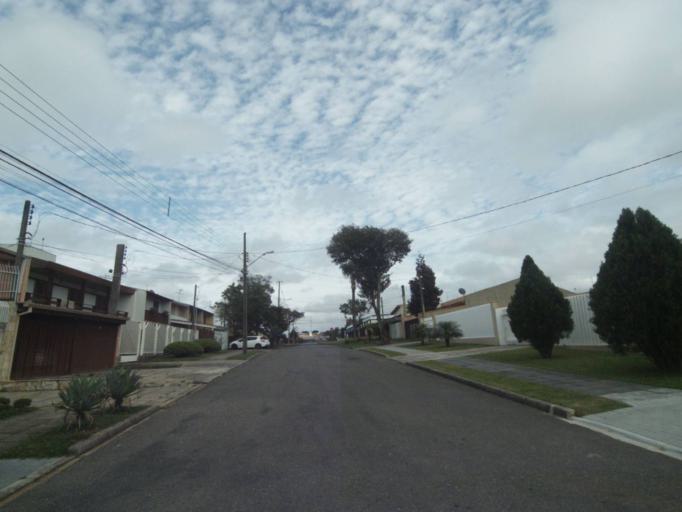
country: BR
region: Parana
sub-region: Pinhais
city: Pinhais
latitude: -25.4338
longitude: -49.2288
